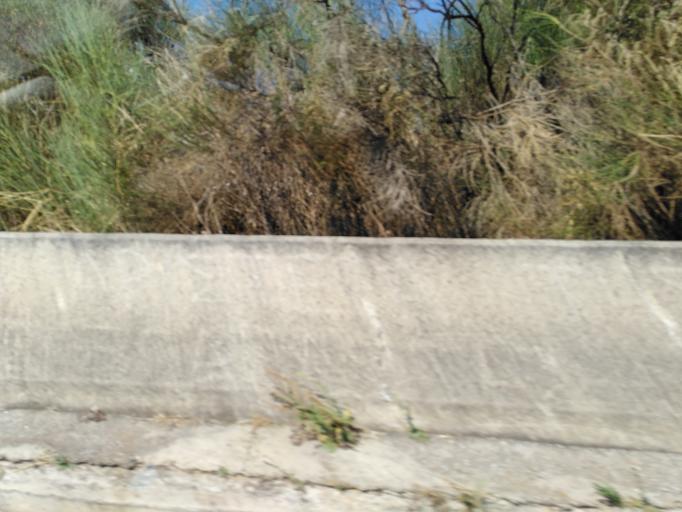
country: GR
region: Central Macedonia
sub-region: Nomos Chalkidikis
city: Nea Kallikrateia
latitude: 40.3023
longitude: 23.1335
